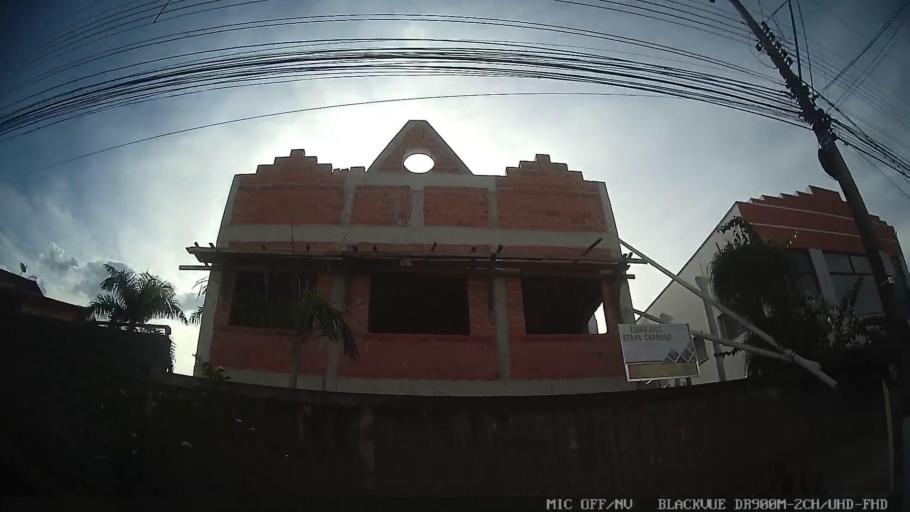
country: BR
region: Sao Paulo
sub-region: Jaguariuna
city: Jaguariuna
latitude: -22.6393
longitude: -47.0525
